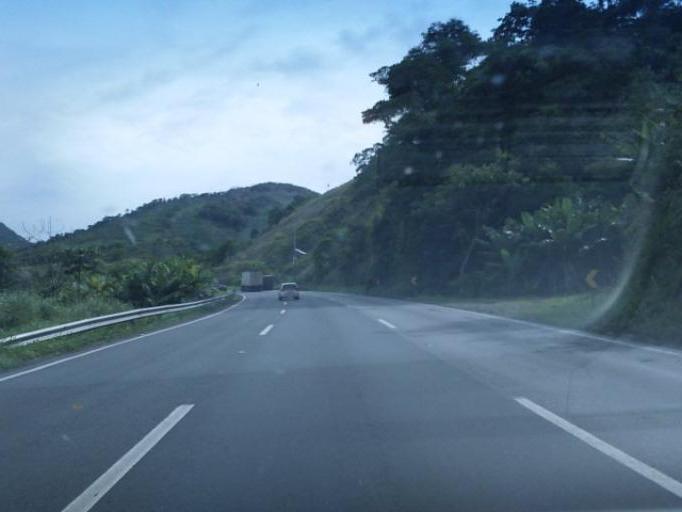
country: BR
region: Sao Paulo
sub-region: Cajati
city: Cajati
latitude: -24.8581
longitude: -48.2171
